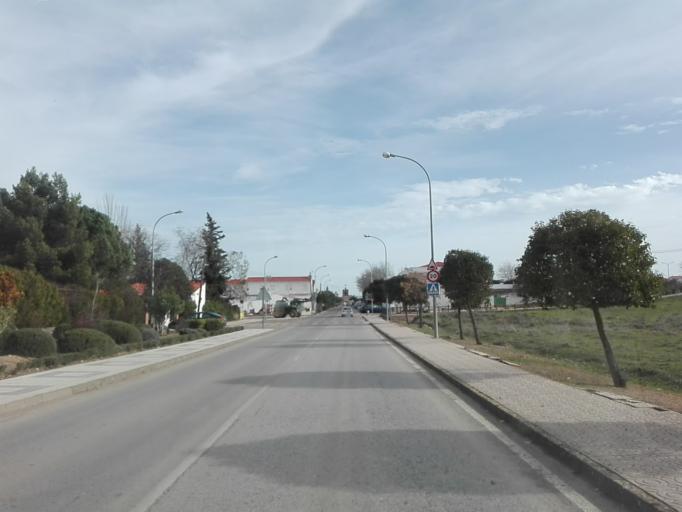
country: ES
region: Extremadura
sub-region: Provincia de Badajoz
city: Llerena
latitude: 38.2345
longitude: -6.0242
